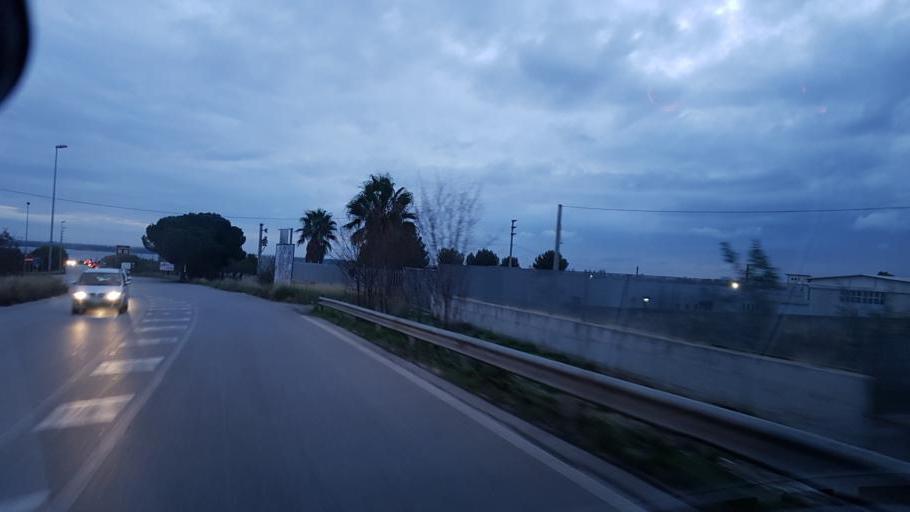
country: IT
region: Apulia
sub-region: Provincia di Taranto
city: Paolo VI
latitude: 40.5140
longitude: 17.2886
